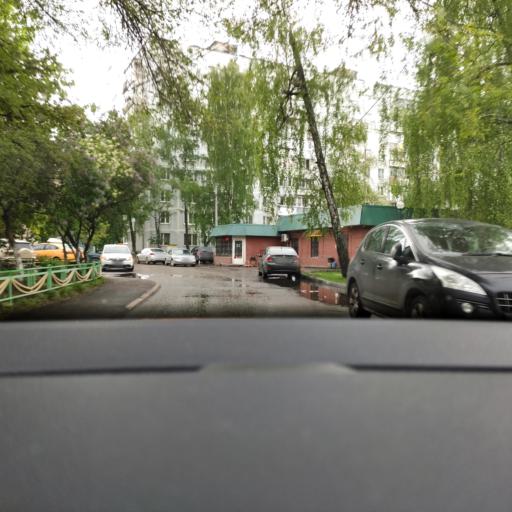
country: RU
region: Moskovskaya
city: Saltykovka
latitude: 55.7317
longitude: 37.9661
